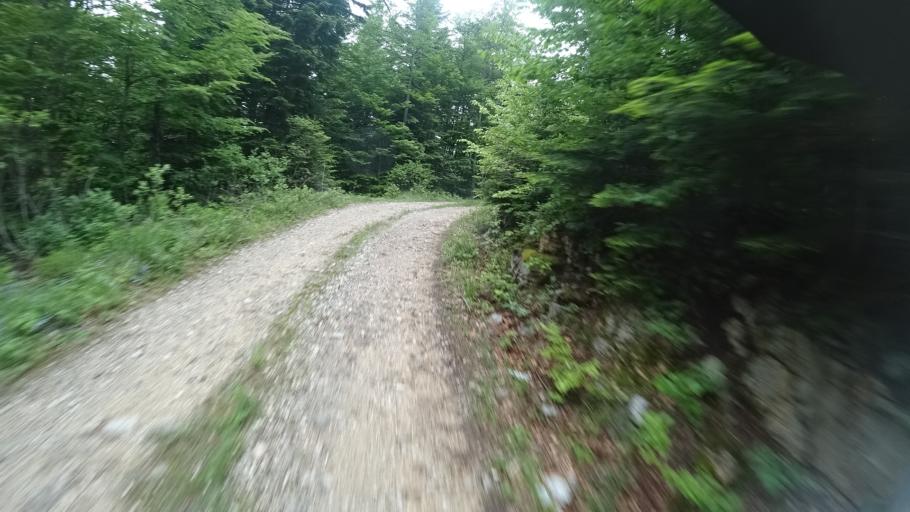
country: BA
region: Federation of Bosnia and Herzegovina
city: Bihac
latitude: 44.6272
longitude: 15.8091
